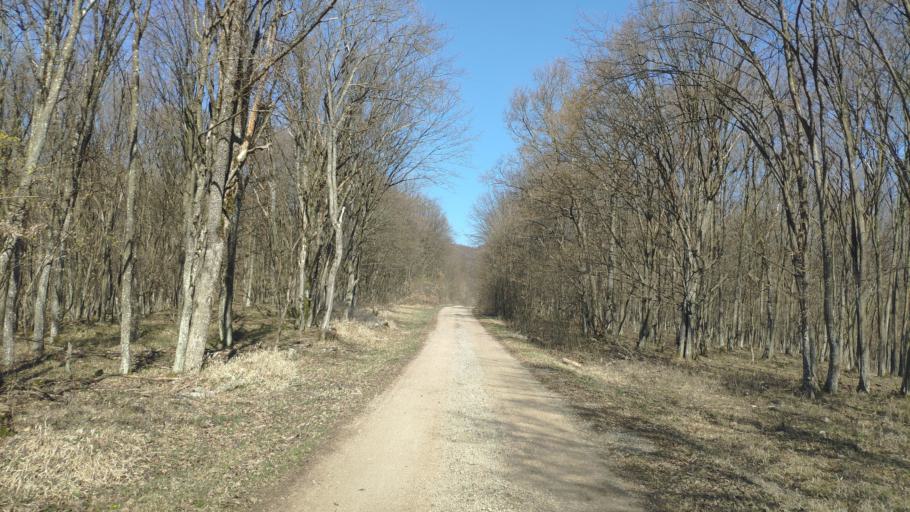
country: SK
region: Kosicky
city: Roznava
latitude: 48.5970
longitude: 20.4113
